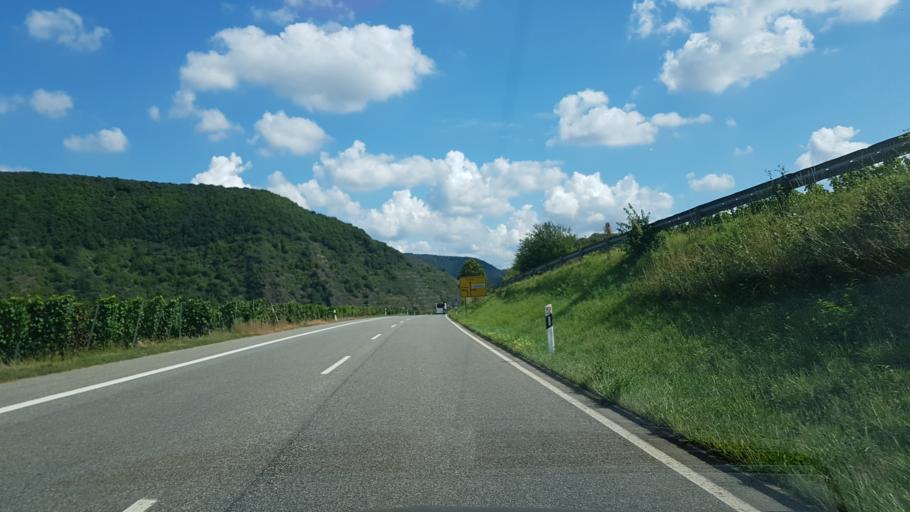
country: DE
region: Rheinland-Pfalz
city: Mesenich
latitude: 50.1075
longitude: 7.2017
